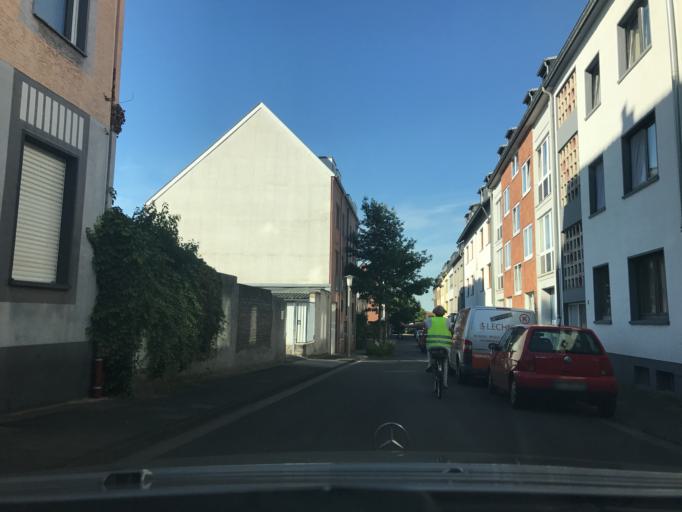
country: DE
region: North Rhine-Westphalia
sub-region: Regierungsbezirk Dusseldorf
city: Krefeld
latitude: 51.3398
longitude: 6.5616
